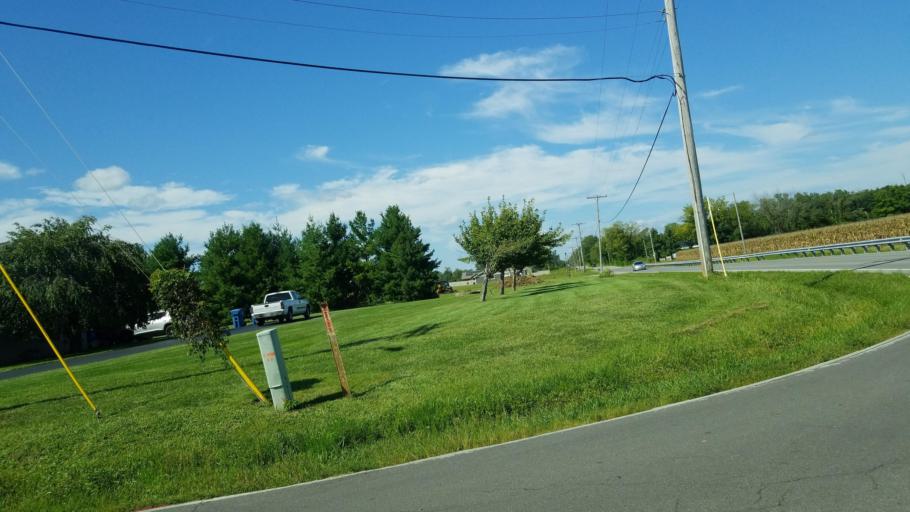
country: US
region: Illinois
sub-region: Williamson County
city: Marion
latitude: 37.7427
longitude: -88.8926
